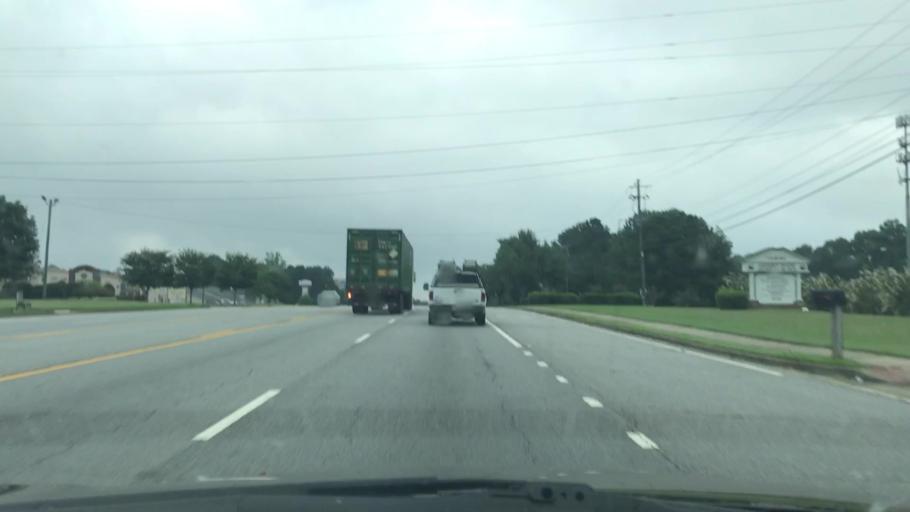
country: US
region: Georgia
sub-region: Gwinnett County
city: Lilburn
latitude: 33.8995
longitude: -84.1337
